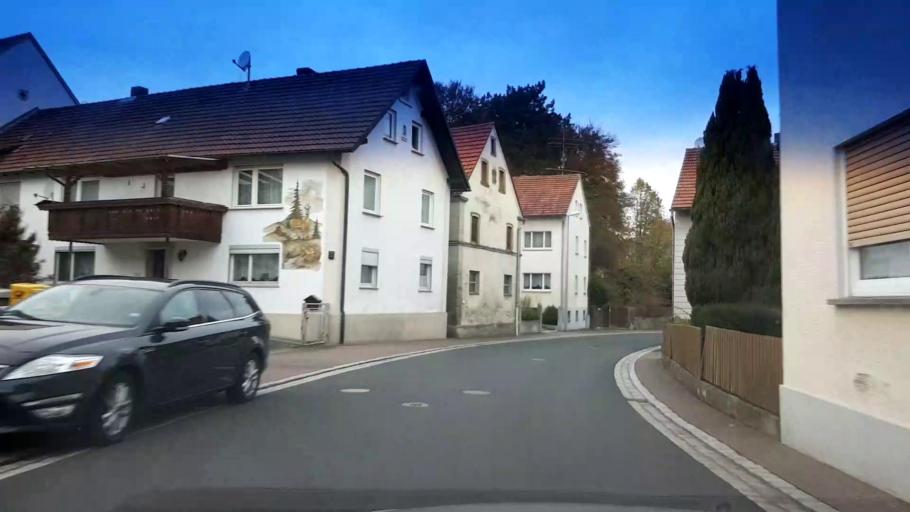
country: DE
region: Bavaria
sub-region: Upper Franconia
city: Priesendorf
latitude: 49.9302
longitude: 10.6939
